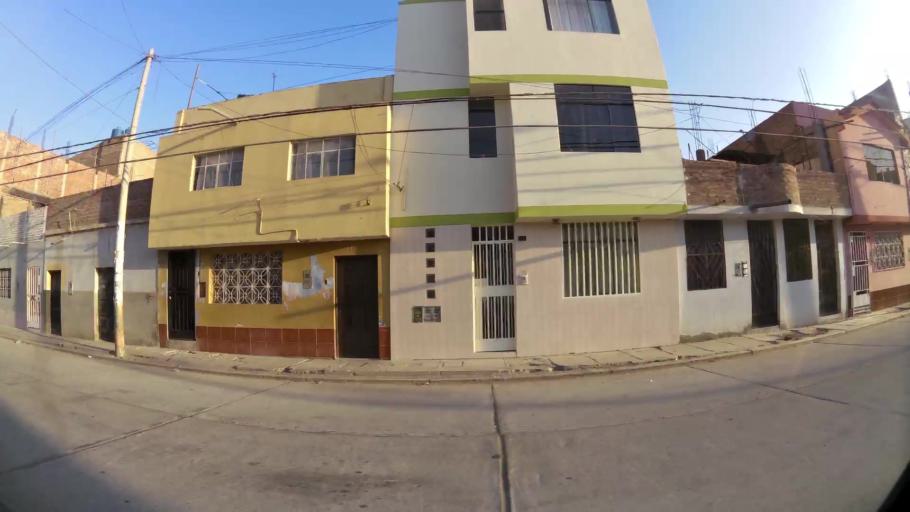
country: PE
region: Lambayeque
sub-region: Provincia de Chiclayo
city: Santa Rosa
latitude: -6.7700
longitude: -79.8303
